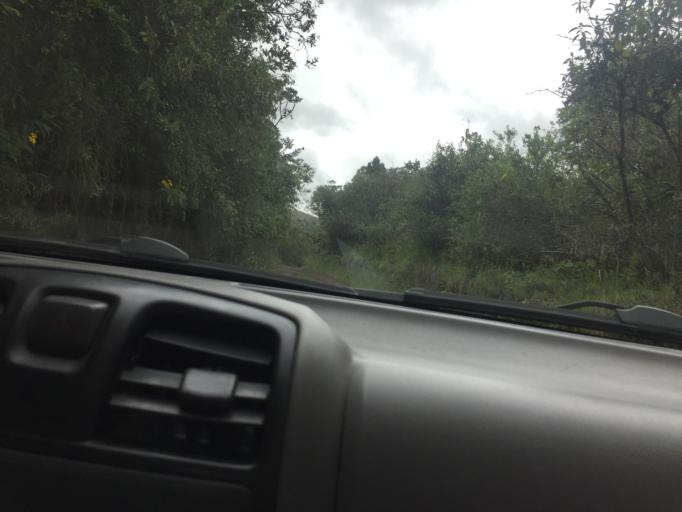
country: EC
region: Pichincha
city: Cayambe
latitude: 0.0733
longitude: -78.3001
